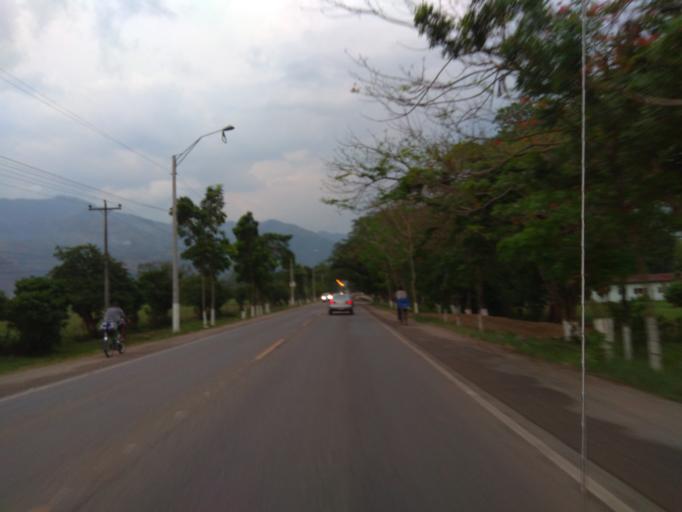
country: HN
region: Yoro
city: El Progreso
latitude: 15.3813
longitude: -87.8044
